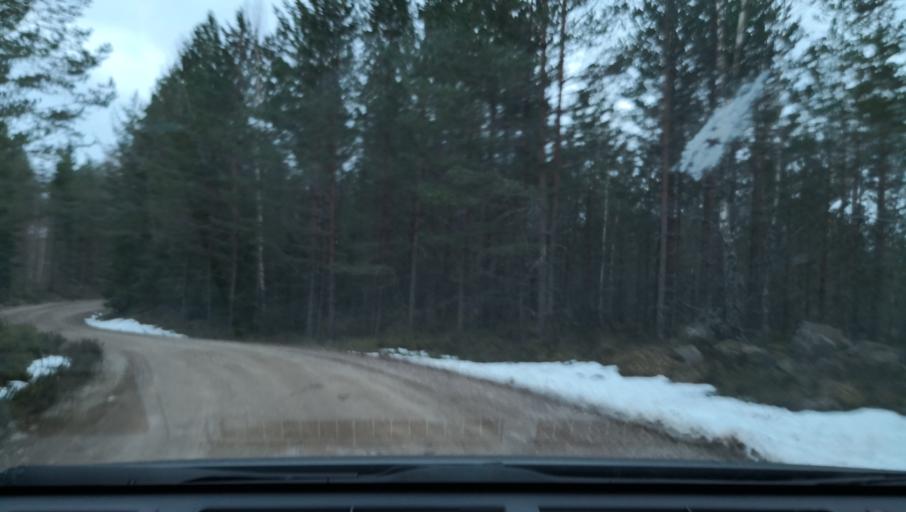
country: SE
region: OErebro
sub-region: Lindesbergs Kommun
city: Fellingsbro
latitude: 59.6082
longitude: 15.5760
